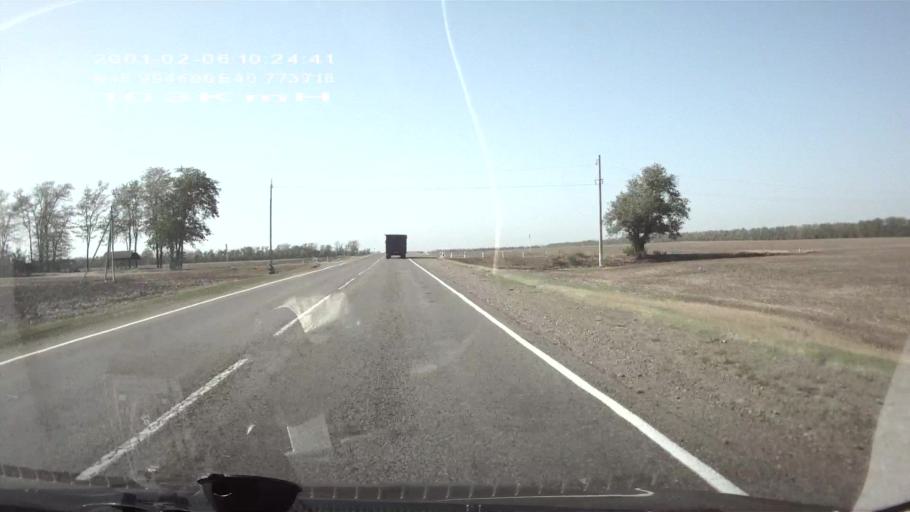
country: RU
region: Krasnodarskiy
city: Novopokrovskaya
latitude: 45.9944
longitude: 40.7736
